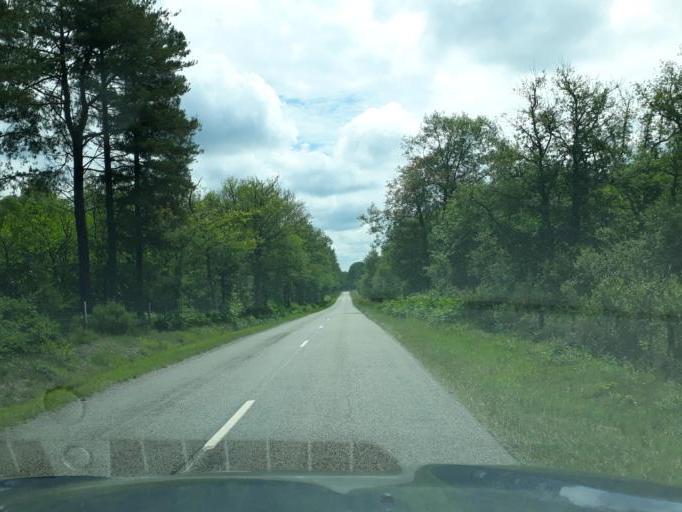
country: FR
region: Centre
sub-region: Departement du Loir-et-Cher
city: Chaumont-sur-Tharonne
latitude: 47.6200
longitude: 1.8814
